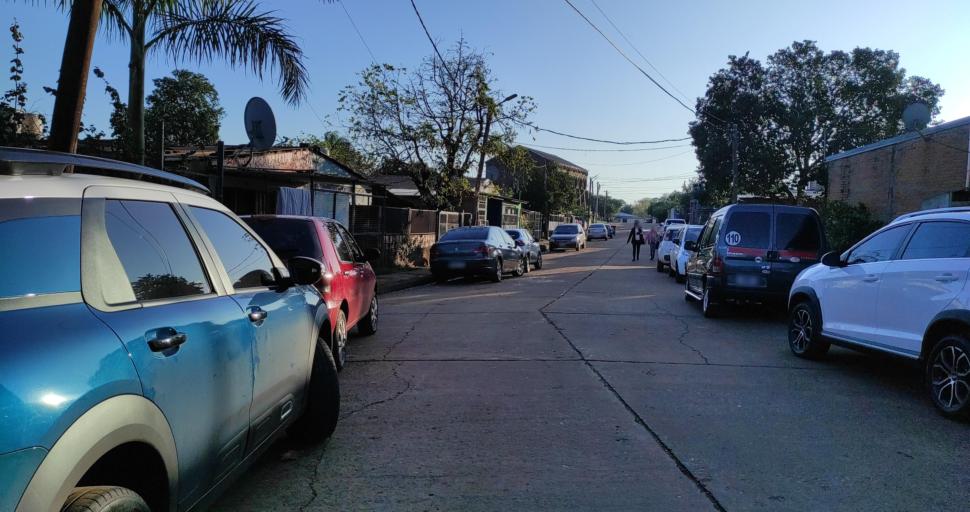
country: AR
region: Misiones
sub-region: Departamento de Capital
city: Posadas
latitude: -27.4177
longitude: -55.9054
